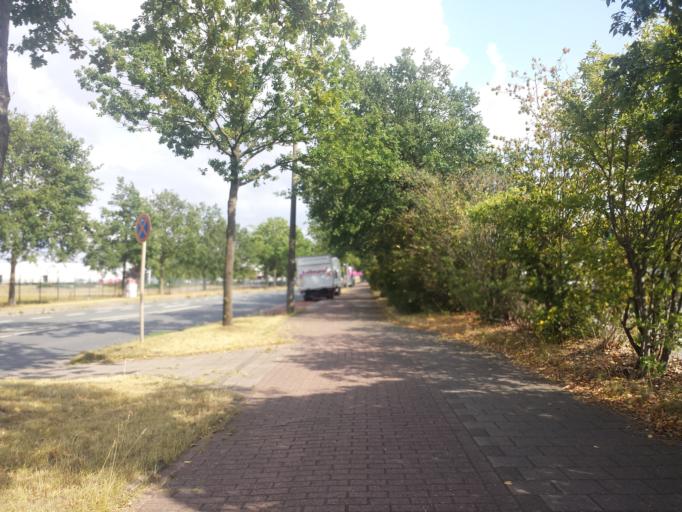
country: DE
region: Lower Saxony
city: Stuhr
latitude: 53.0852
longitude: 8.7182
